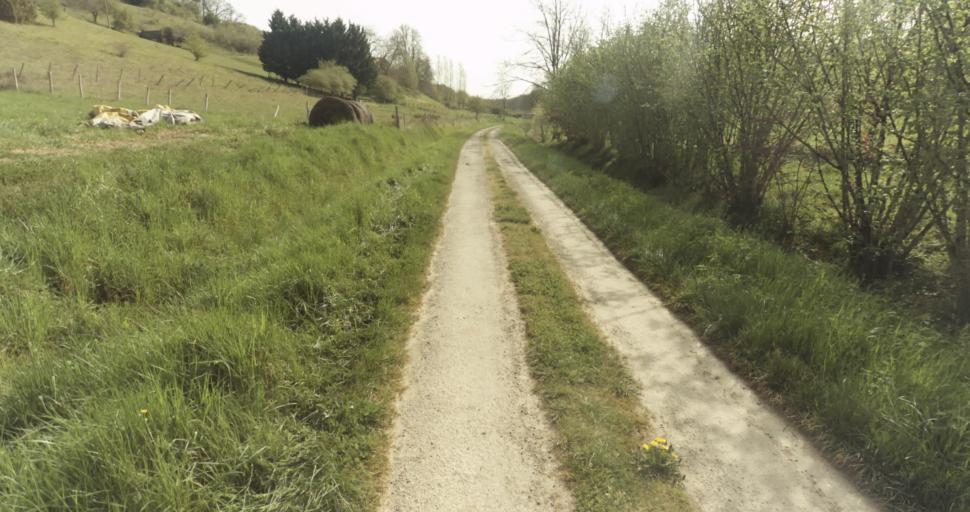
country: FR
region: Midi-Pyrenees
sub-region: Departement du Tarn-et-Garonne
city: Moissac
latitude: 44.1263
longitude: 1.0840
